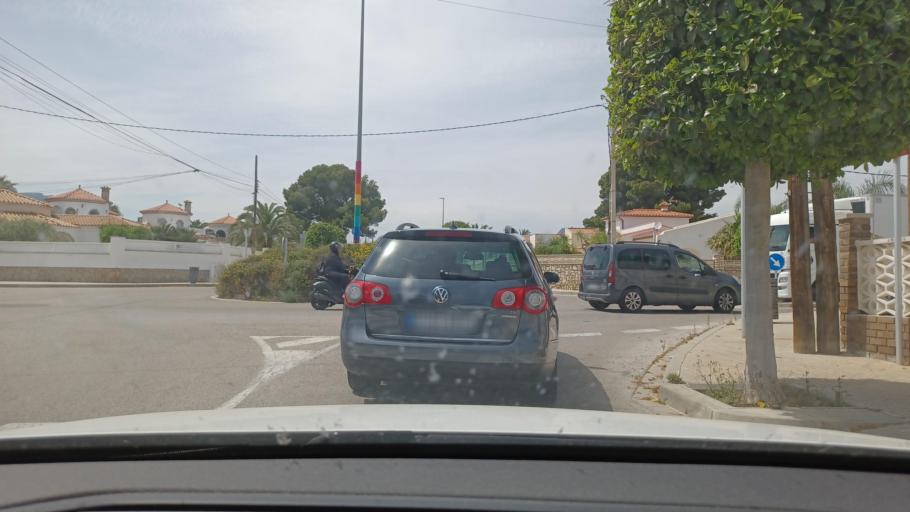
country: ES
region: Catalonia
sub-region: Provincia de Tarragona
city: Colldejou
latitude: 41.0069
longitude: 0.9297
